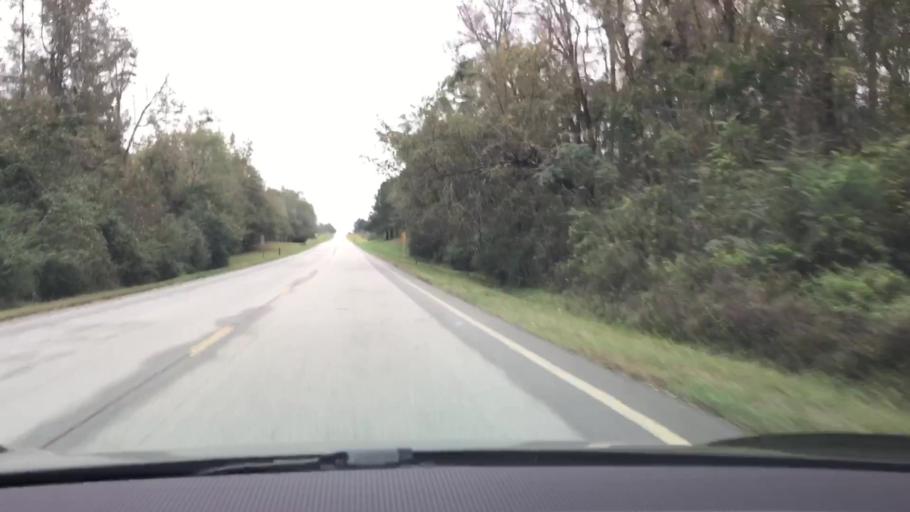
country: US
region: Georgia
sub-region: Jefferson County
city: Wrens
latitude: 33.2377
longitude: -82.4564
